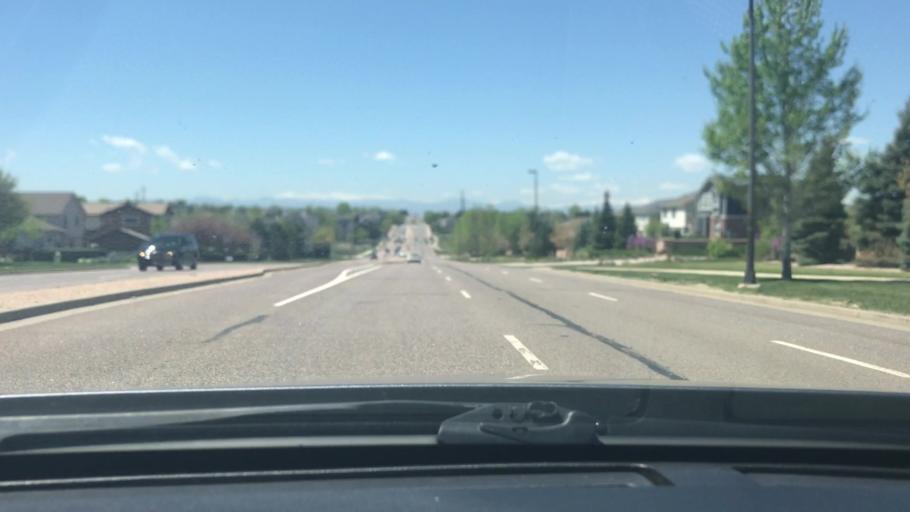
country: US
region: Colorado
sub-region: Arapahoe County
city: Dove Valley
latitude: 39.6530
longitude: -104.7467
